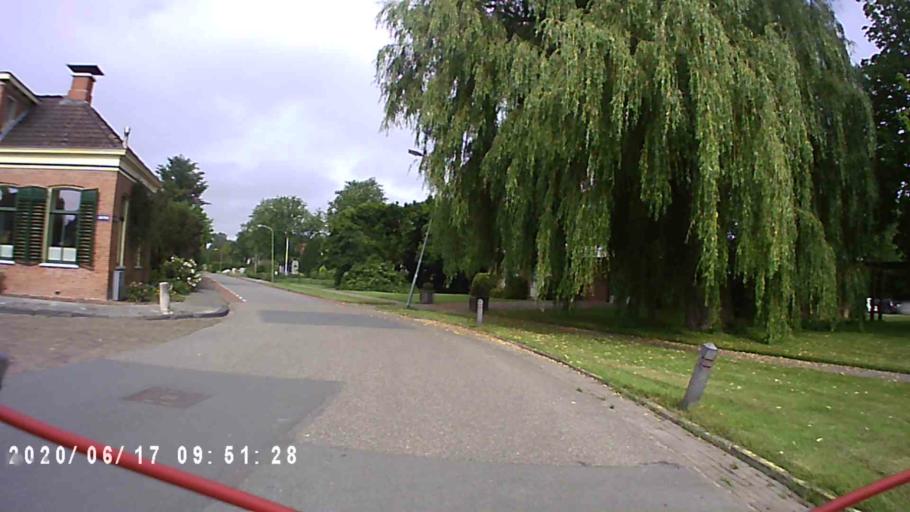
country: NL
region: Groningen
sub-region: Gemeente De Marne
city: Ulrum
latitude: 53.3597
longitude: 6.3294
